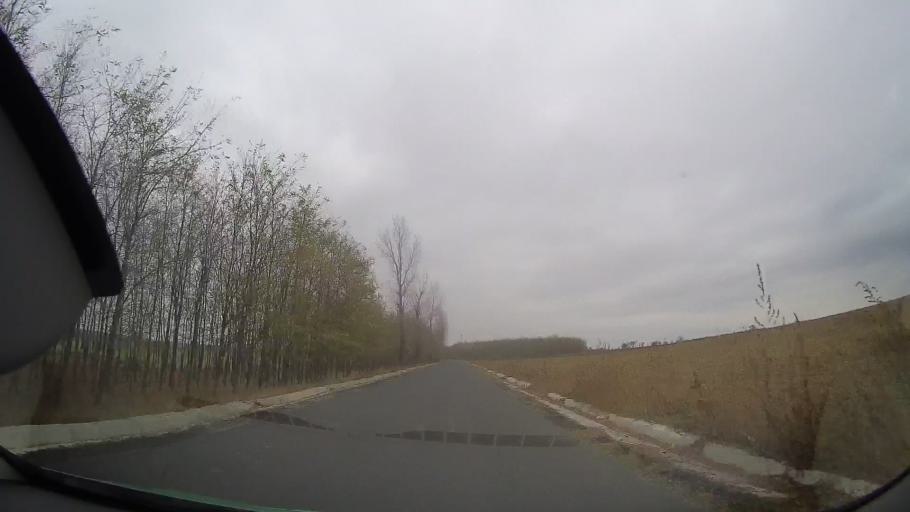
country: RO
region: Braila
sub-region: Comuna Ciocile
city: Ciocile
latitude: 44.7940
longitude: 27.2759
